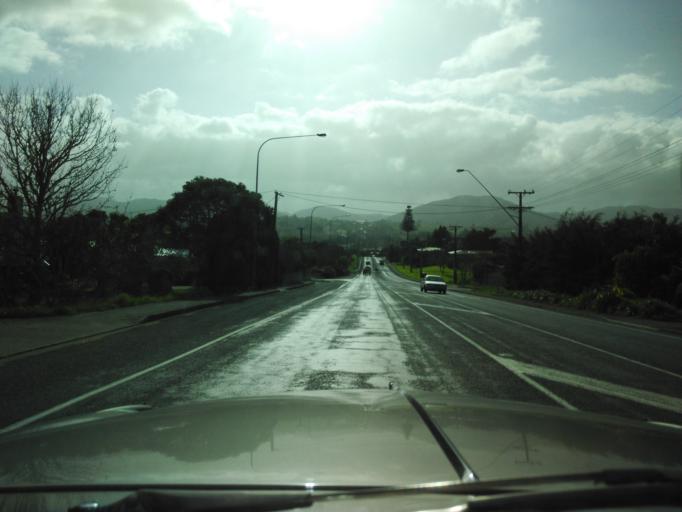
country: NZ
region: Auckland
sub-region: Auckland
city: Wellsford
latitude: -36.1710
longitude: 174.4471
